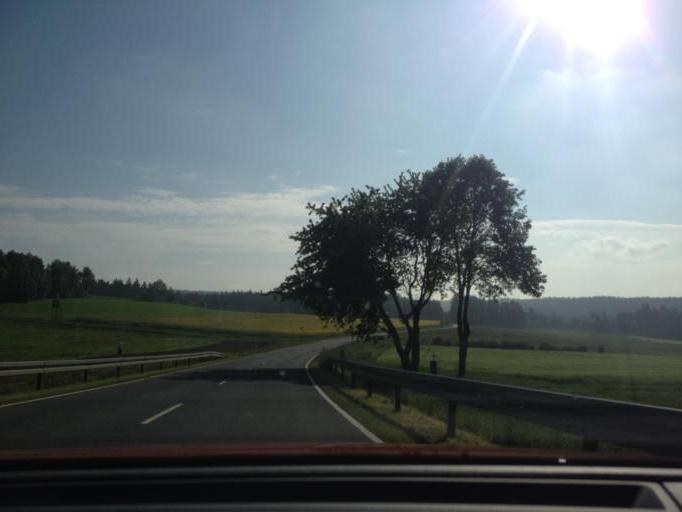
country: DE
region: Bavaria
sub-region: Upper Franconia
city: Creussen
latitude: 49.7690
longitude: 11.6167
